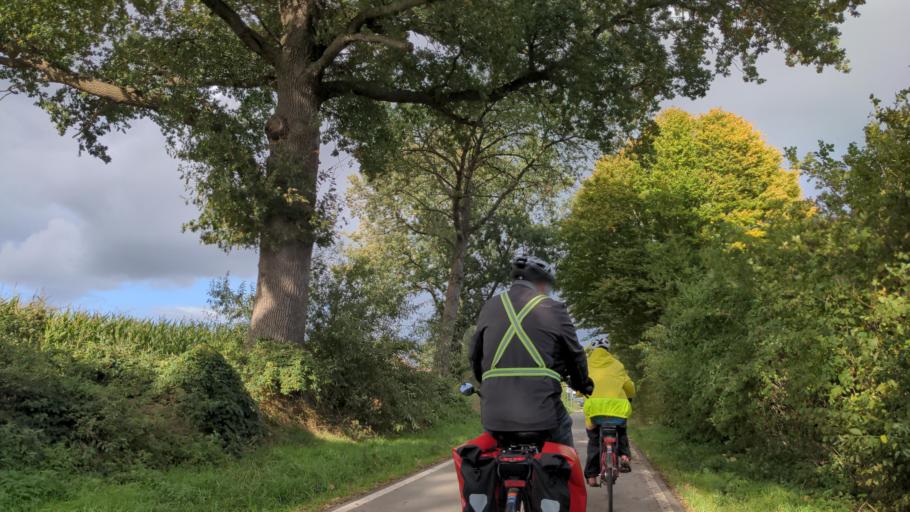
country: DE
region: Schleswig-Holstein
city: Hamberge
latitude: 53.8129
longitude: 10.6155
